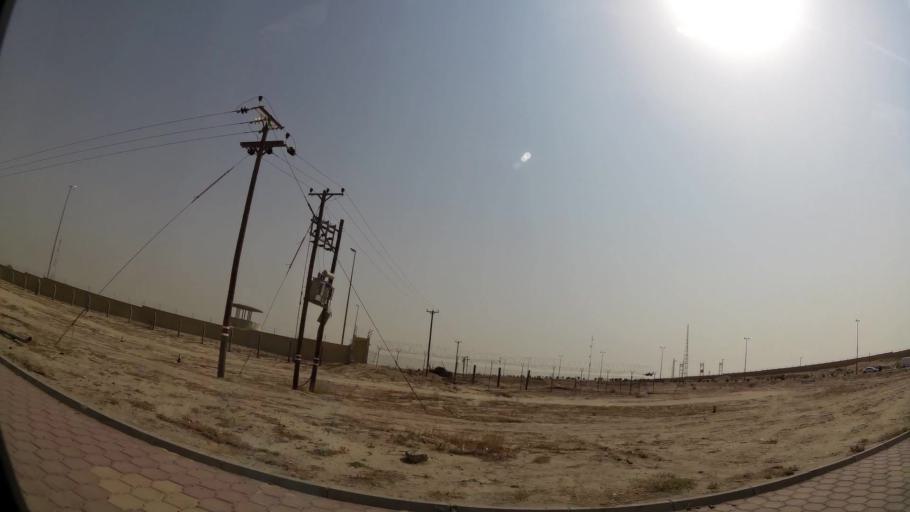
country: KW
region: Muhafazat al Jahra'
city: Al Jahra'
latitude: 29.3266
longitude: 47.7022
